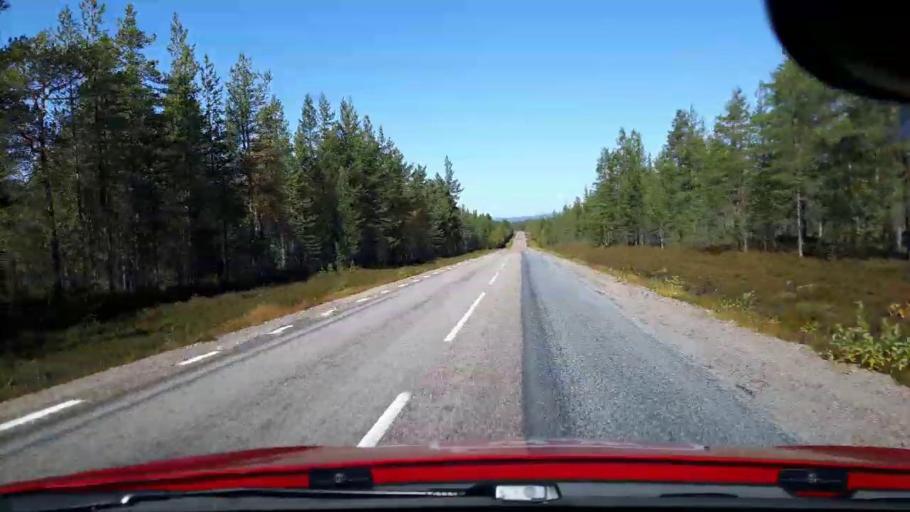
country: SE
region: Jaemtland
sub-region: Harjedalens Kommun
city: Sveg
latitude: 61.7321
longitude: 14.1645
